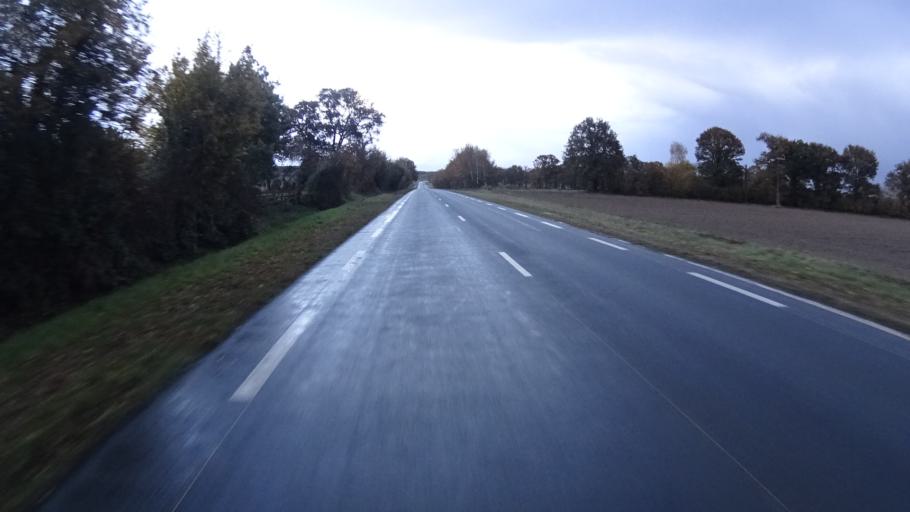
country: FR
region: Brittany
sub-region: Departement d'Ille-et-Vilaine
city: Bains-sur-Oust
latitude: 47.6910
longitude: -2.0481
